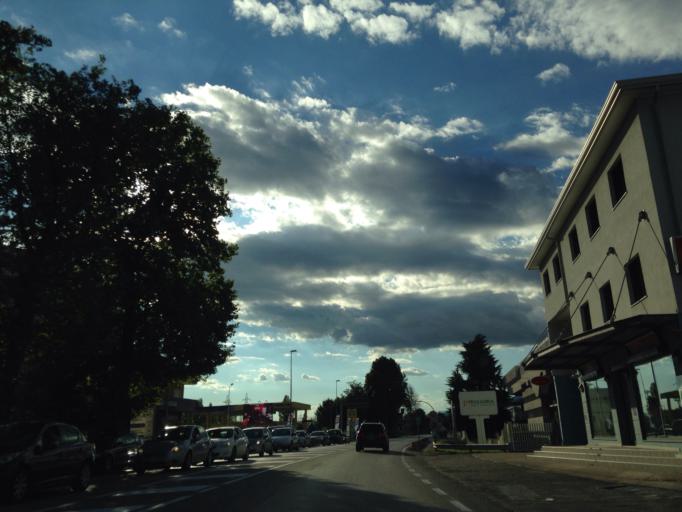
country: IT
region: Friuli Venezia Giulia
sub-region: Provincia di Pordenone
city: Porcia
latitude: 45.9679
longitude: 12.6256
